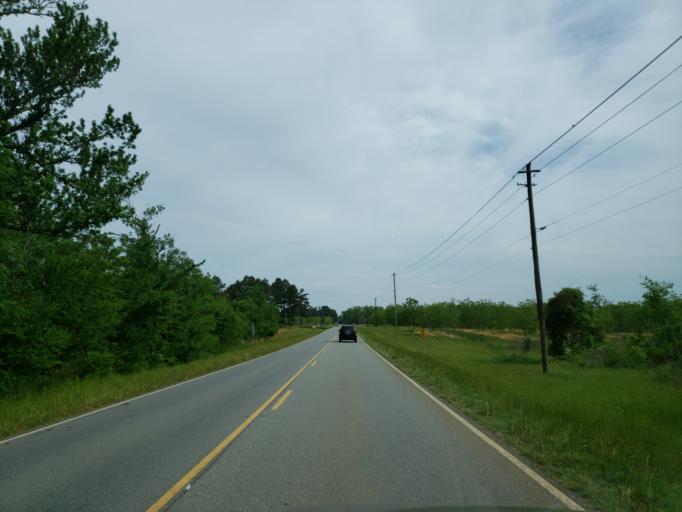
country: US
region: Georgia
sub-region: Dooly County
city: Vienna
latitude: 32.1590
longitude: -83.8834
